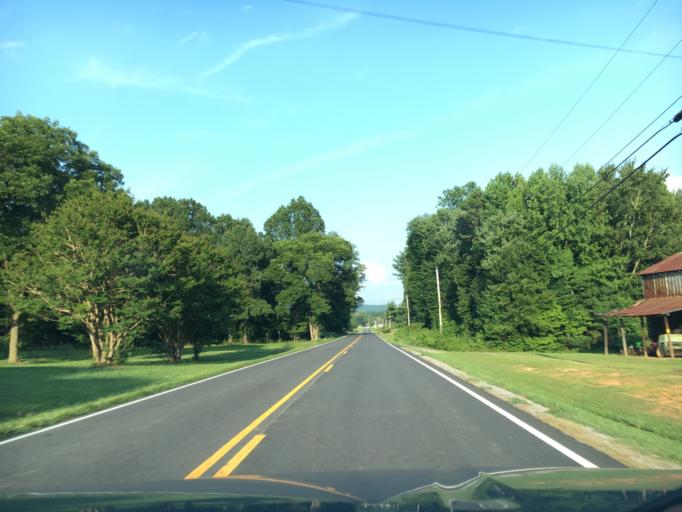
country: US
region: Virginia
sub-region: Pittsylvania County
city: Chatham
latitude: 36.8180
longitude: -79.3561
